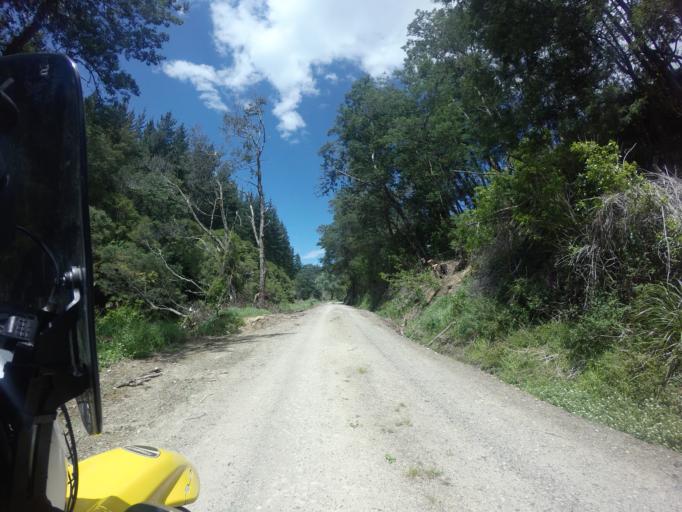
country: NZ
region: Hawke's Bay
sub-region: Wairoa District
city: Wairoa
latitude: -38.9702
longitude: 177.6703
